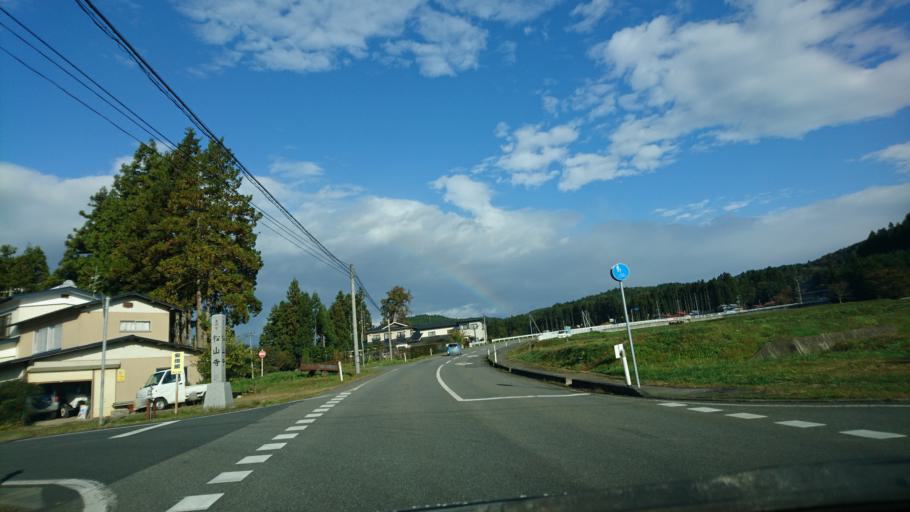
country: JP
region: Iwate
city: Mizusawa
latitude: 39.0407
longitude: 141.0612
